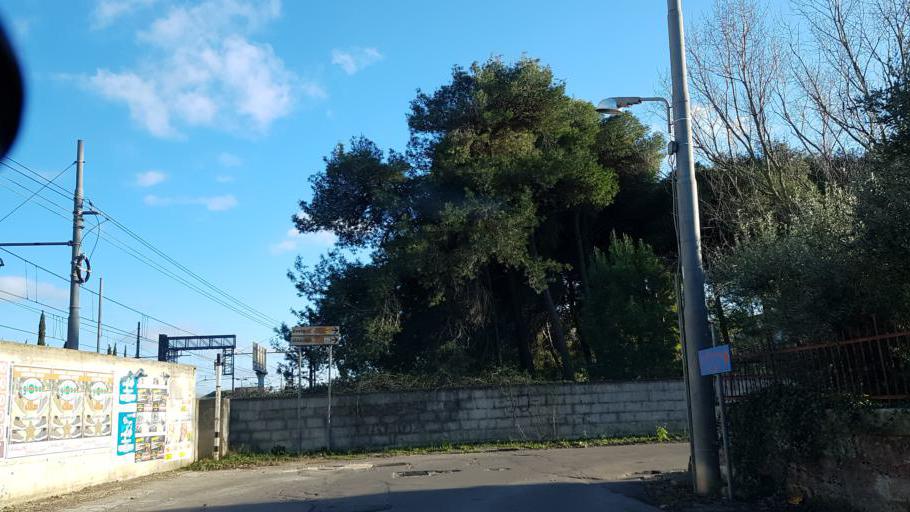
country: IT
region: Apulia
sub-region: Provincia di Lecce
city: Squinzano
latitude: 40.4423
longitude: 18.0426
